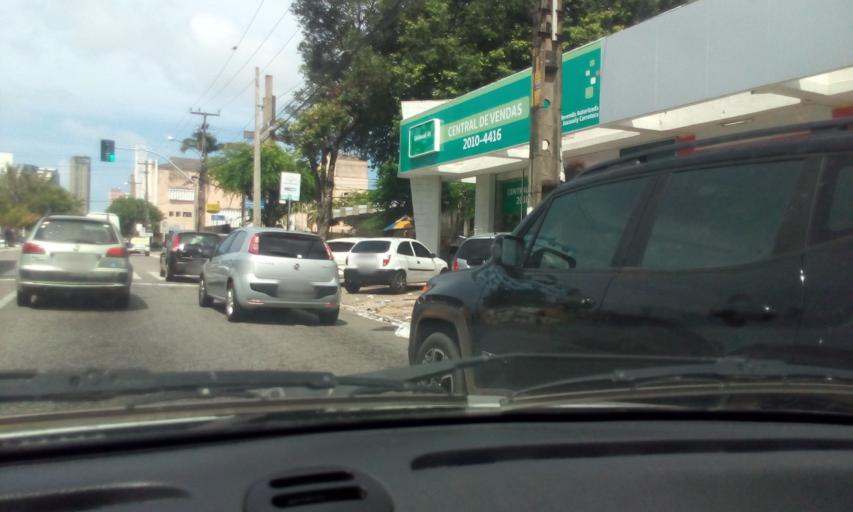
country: BR
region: Rio Grande do Norte
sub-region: Natal
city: Natal
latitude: -5.7887
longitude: -35.2046
